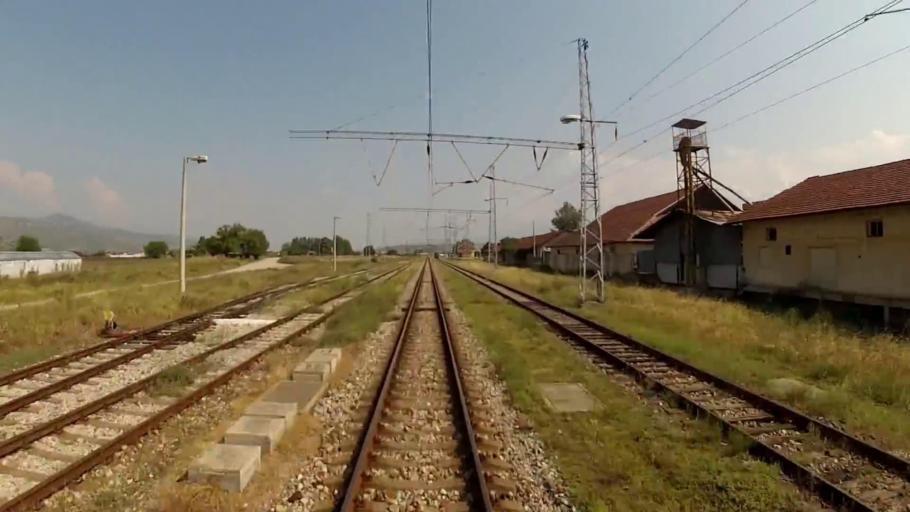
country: BG
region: Blagoevgrad
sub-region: Obshtina Sandanski
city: Sandanski
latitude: 41.5048
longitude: 23.2699
